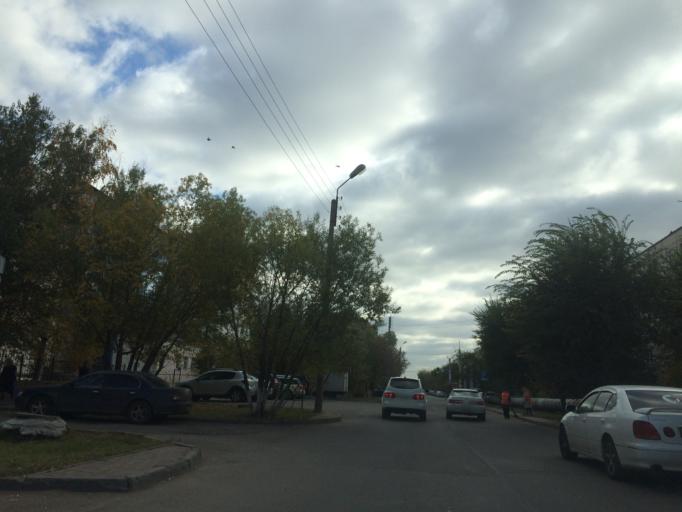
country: KZ
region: Astana Qalasy
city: Astana
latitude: 51.1715
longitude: 71.4148
